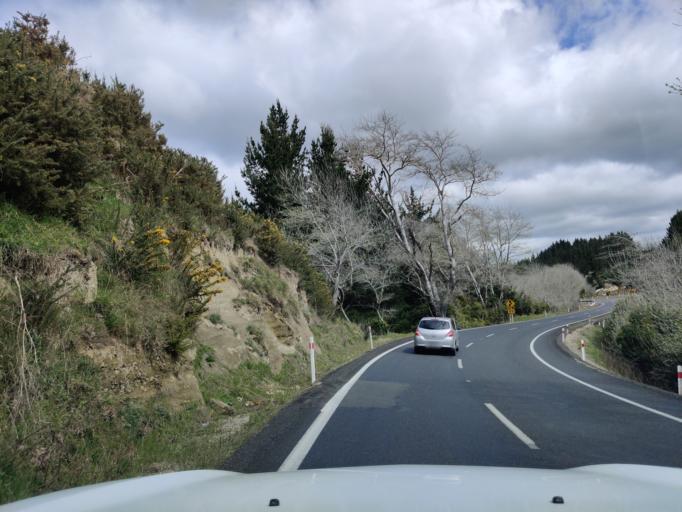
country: NZ
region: Manawatu-Wanganui
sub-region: Wanganui District
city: Wanganui
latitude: -39.7926
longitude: 175.2111
